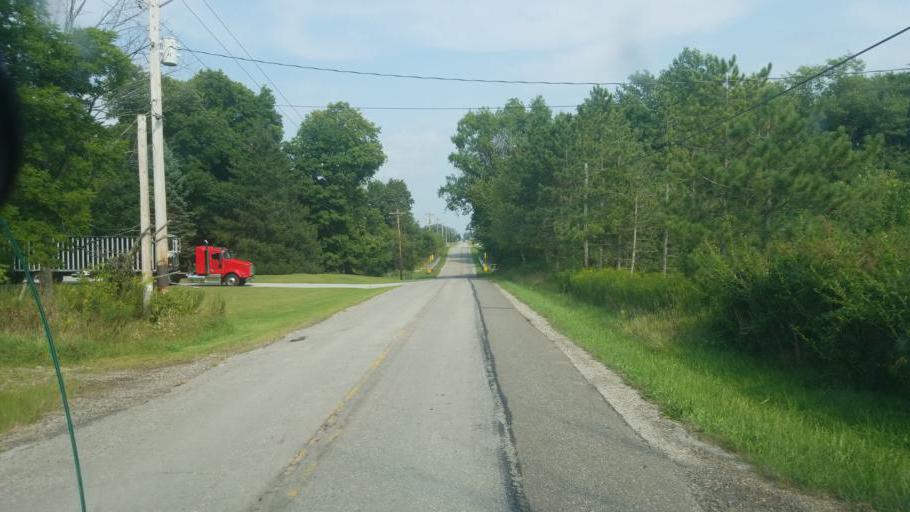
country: US
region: Ohio
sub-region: Medina County
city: Lodi
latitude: 41.1361
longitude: -82.0341
